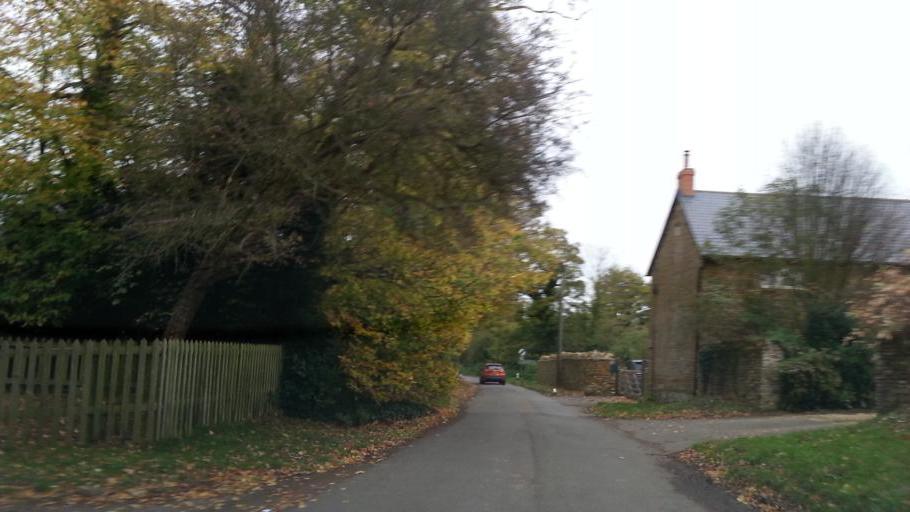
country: GB
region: England
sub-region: Northamptonshire
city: Desborough
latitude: 52.4857
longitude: -0.8142
